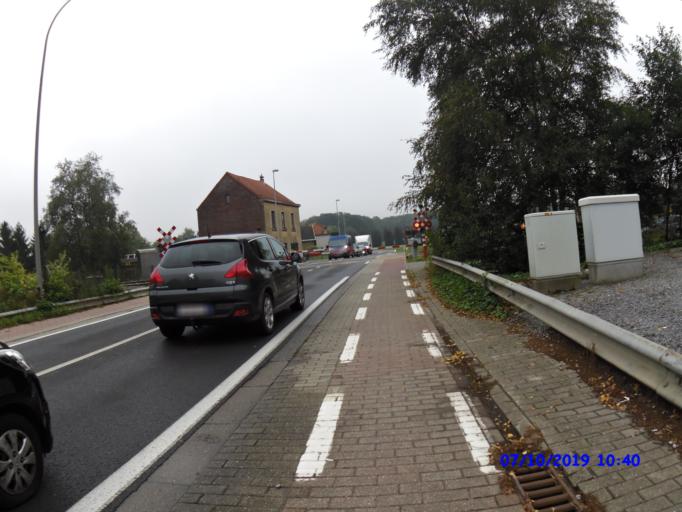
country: BE
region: Flanders
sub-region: Provincie Oost-Vlaanderen
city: Melle
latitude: 50.9804
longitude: 3.8015
